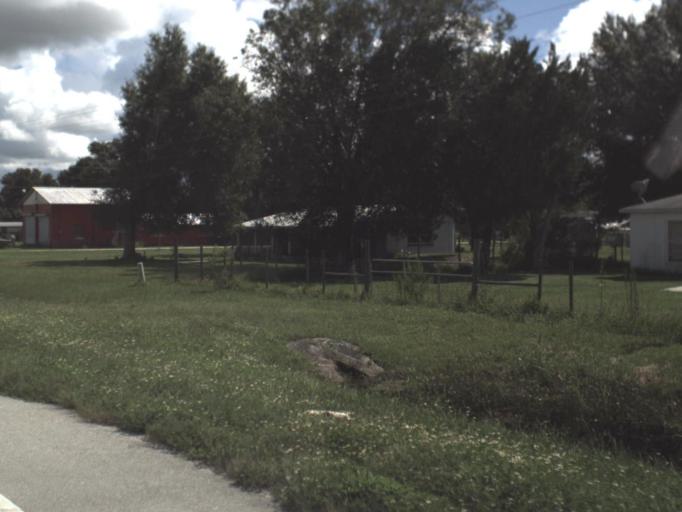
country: US
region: Florida
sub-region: DeSoto County
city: Arcadia
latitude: 27.2311
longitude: -81.9151
